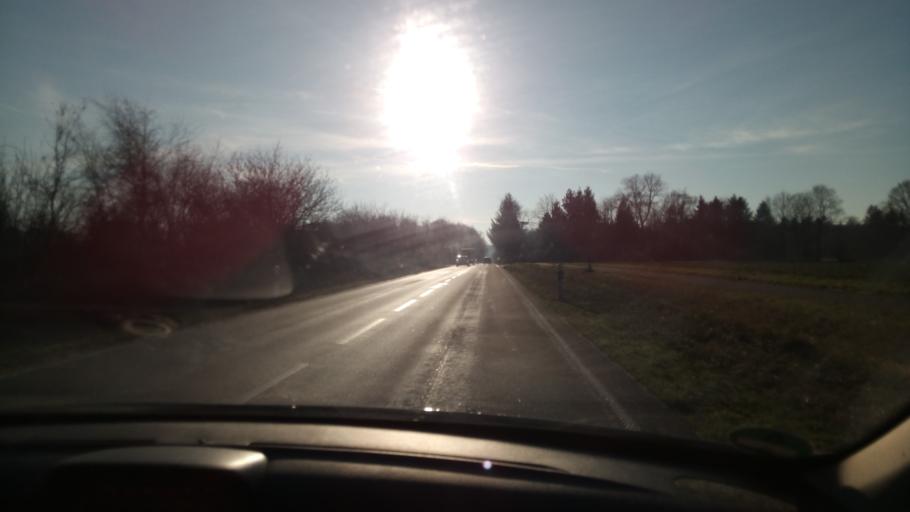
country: DE
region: Schleswig-Holstein
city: Dalldorf
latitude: 53.4411
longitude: 10.6070
